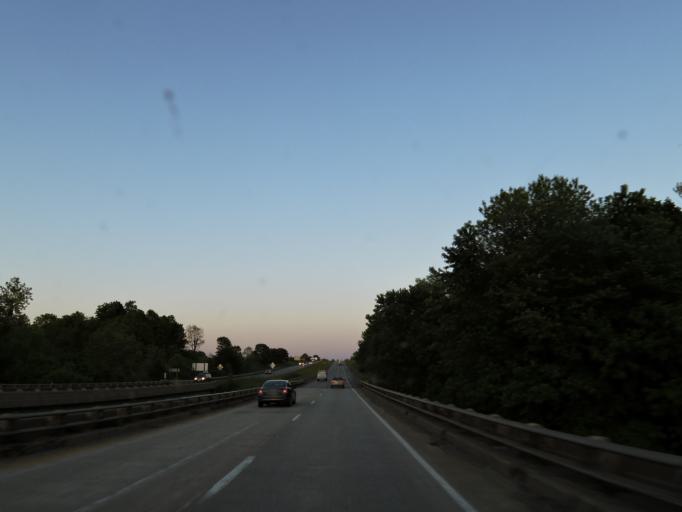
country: US
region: Indiana
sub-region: Montgomery County
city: Crawfordsville
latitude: 40.0760
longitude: -86.8890
